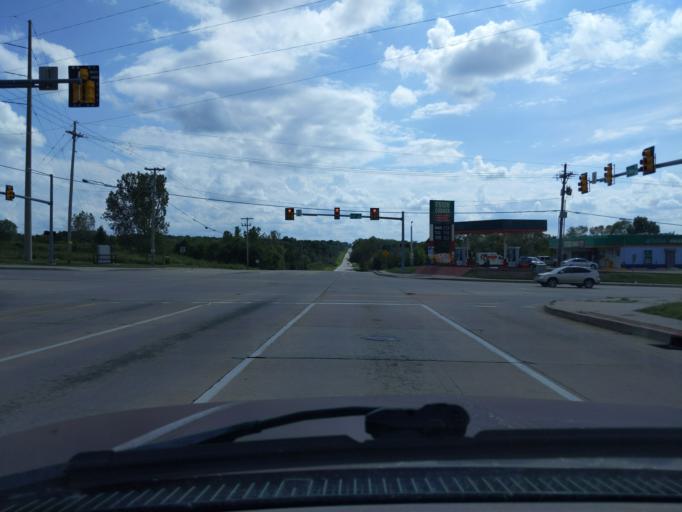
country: US
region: Oklahoma
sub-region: Tulsa County
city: Oakhurst
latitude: 36.0757
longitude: -96.0118
